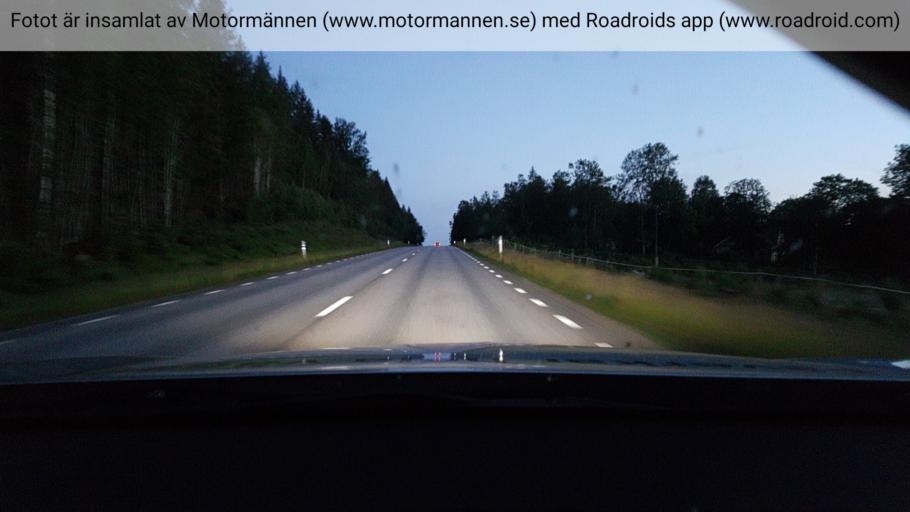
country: SE
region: Vaestra Goetaland
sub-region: Karlsborgs Kommun
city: Molltorp
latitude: 58.4612
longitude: 14.2837
